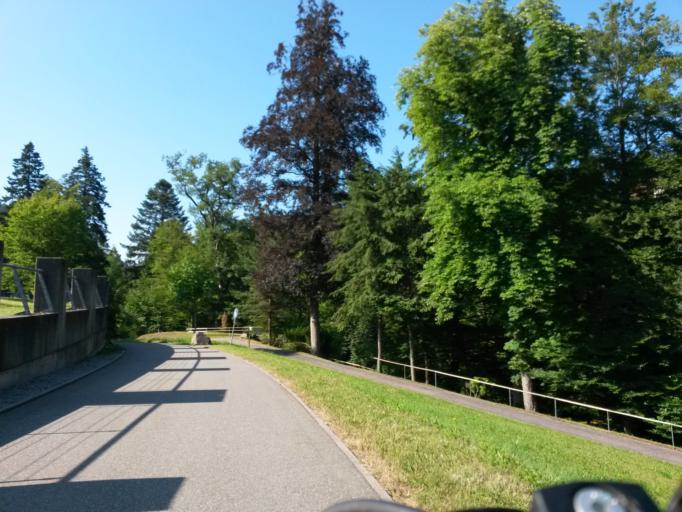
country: DE
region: Baden-Wuerttemberg
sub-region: Karlsruhe Region
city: Bad Wildbad
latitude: 48.7457
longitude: 8.5472
